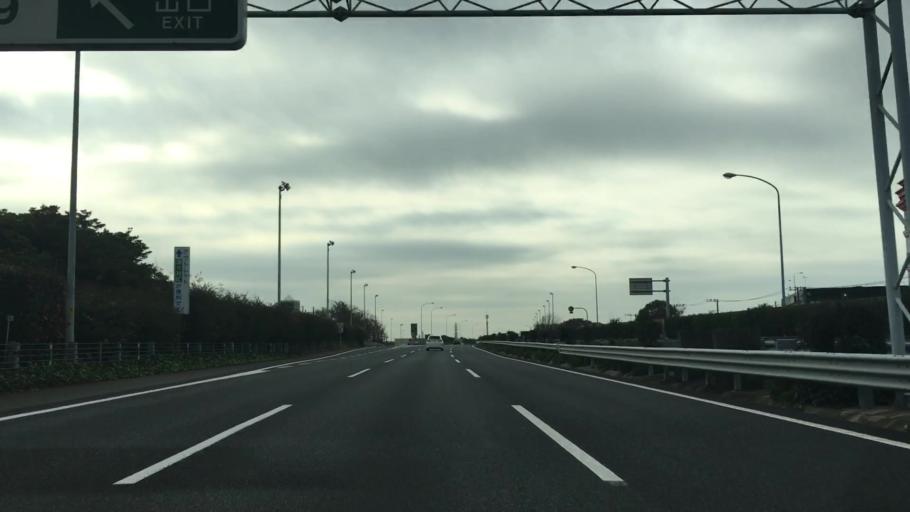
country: JP
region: Chiba
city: Narita
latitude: 35.7492
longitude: 140.3159
